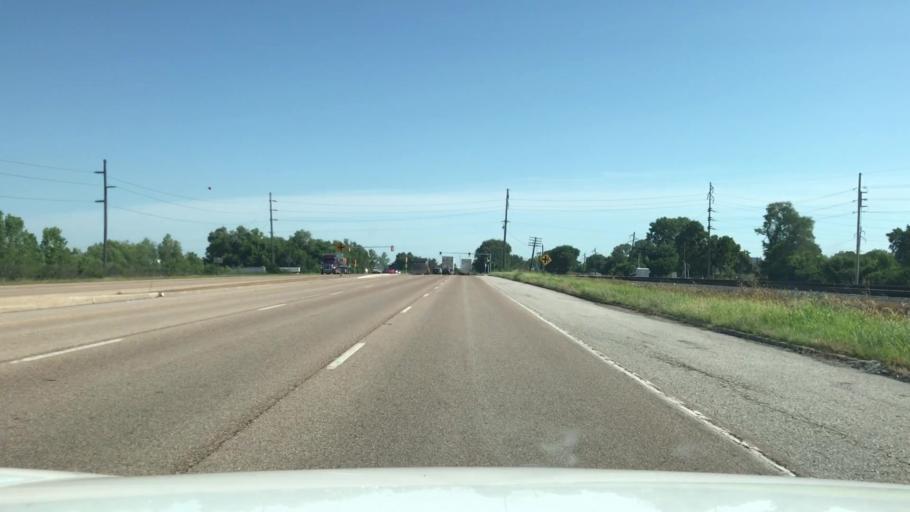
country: US
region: Illinois
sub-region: Madison County
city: Venice
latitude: 38.6782
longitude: -90.1737
